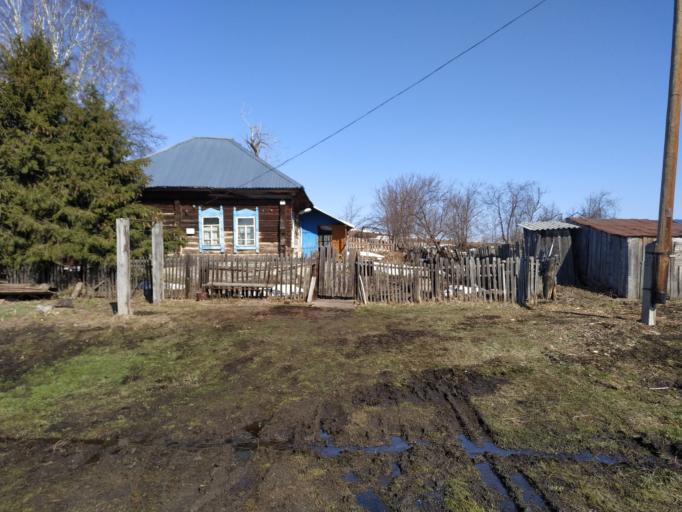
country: RU
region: Altai Krai
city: Krasnogorskoye
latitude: 52.4803
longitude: 86.2169
